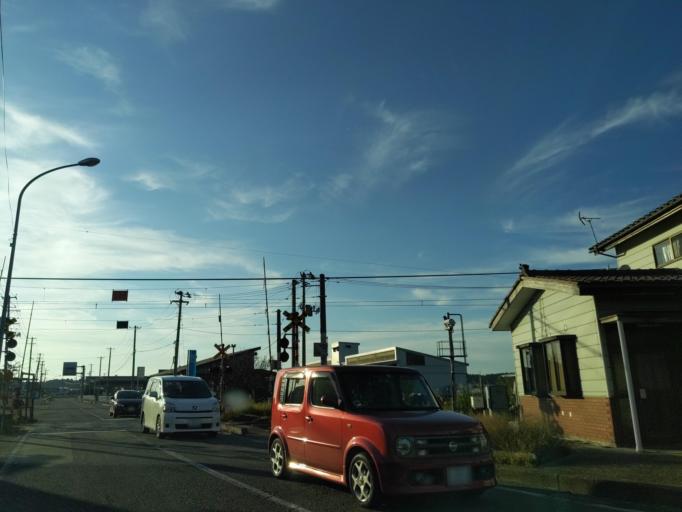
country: JP
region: Niigata
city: Yoshida-kasugacho
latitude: 37.5806
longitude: 138.7823
